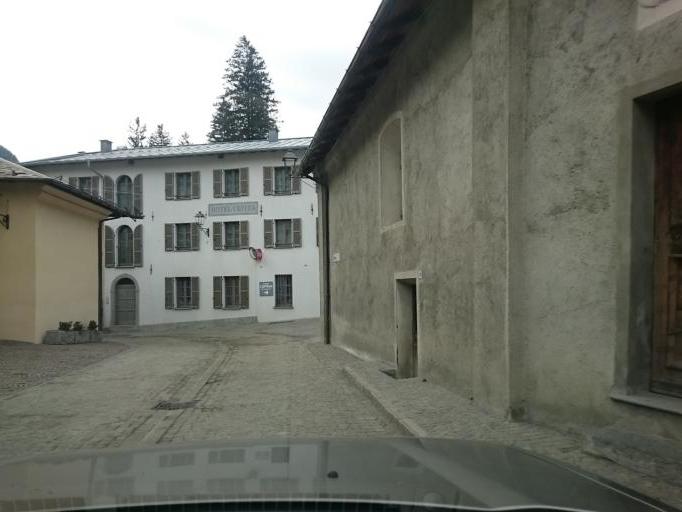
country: IT
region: Lombardy
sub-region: Provincia di Sondrio
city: Valdisotto
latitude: 46.4281
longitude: 10.3558
